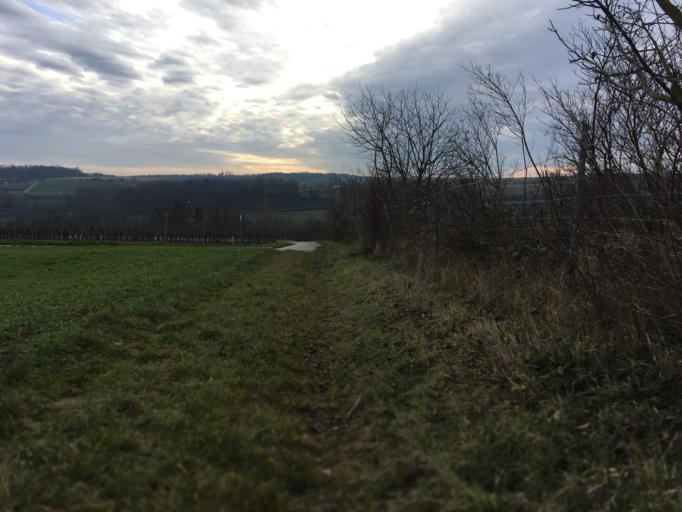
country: DE
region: Baden-Wuerttemberg
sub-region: Regierungsbezirk Stuttgart
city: Ilsfeld
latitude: 49.0578
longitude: 9.2182
